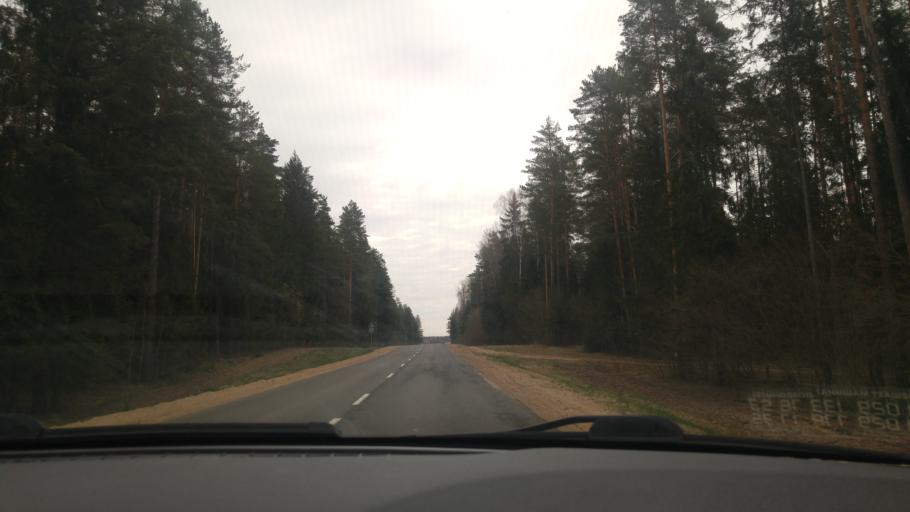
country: BY
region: Minsk
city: Chervyen'
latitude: 53.7370
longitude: 28.3098
